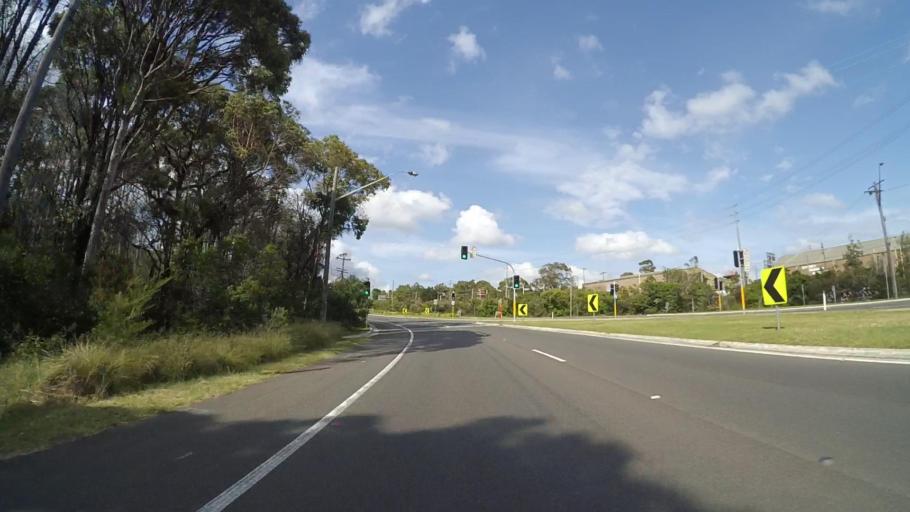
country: AU
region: New South Wales
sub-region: Sutherland Shire
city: Loftus
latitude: -34.0452
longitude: 151.0531
